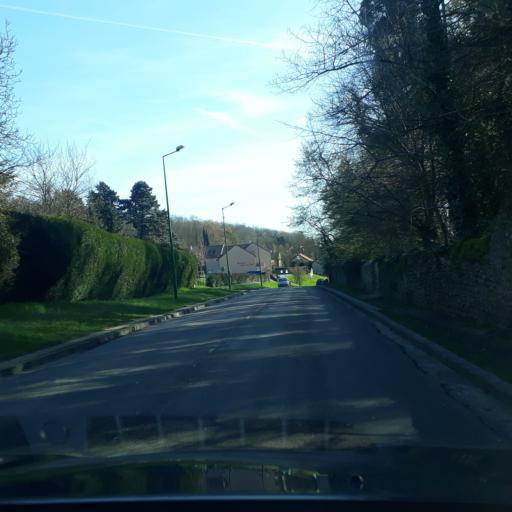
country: FR
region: Ile-de-France
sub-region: Departement de l'Essonne
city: La Ferte-Alais
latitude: 48.4868
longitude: 2.3411
